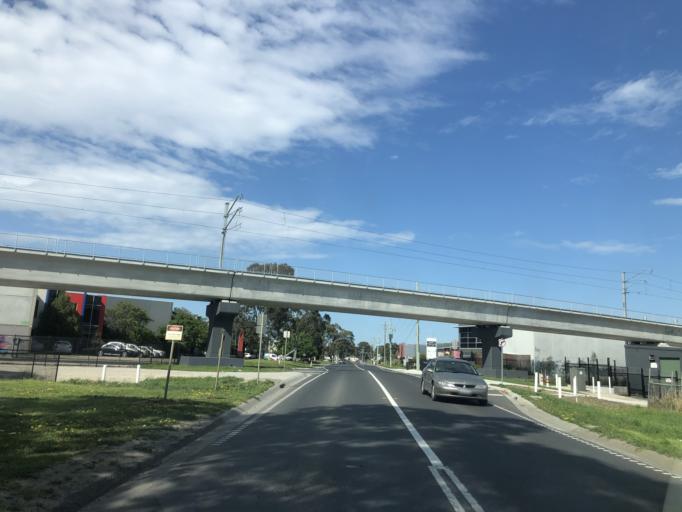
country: AU
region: Victoria
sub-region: Casey
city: Hampton Park
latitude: -38.0348
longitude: 145.2377
